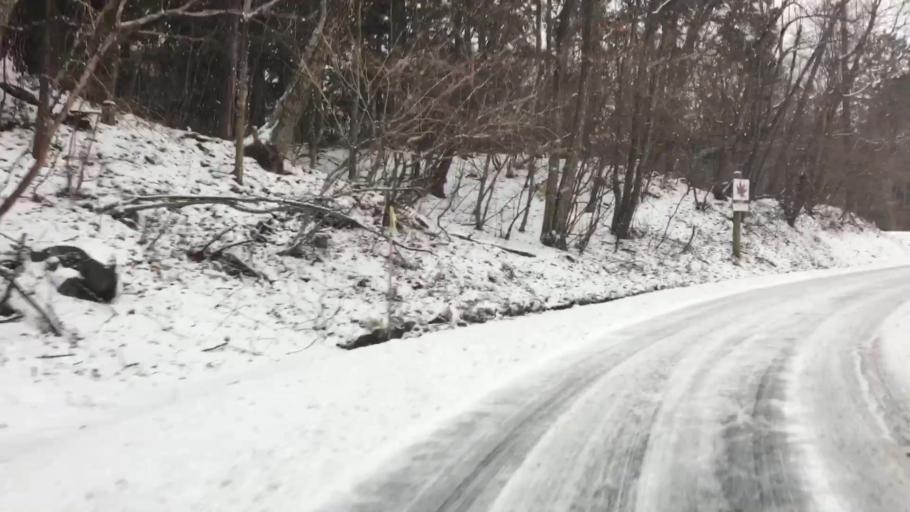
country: JP
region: Tochigi
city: Imaichi
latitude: 36.8801
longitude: 139.7241
